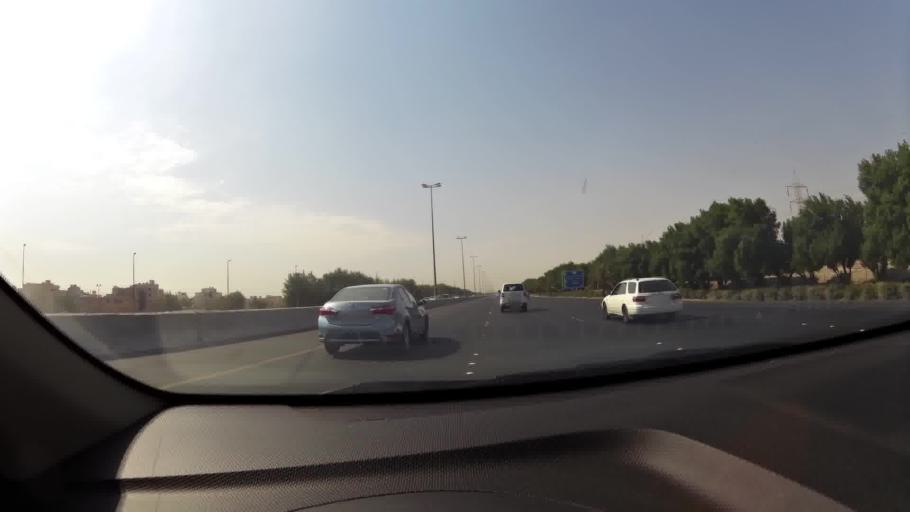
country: KW
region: Mubarak al Kabir
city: Sabah as Salim
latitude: 29.2185
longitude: 48.0560
